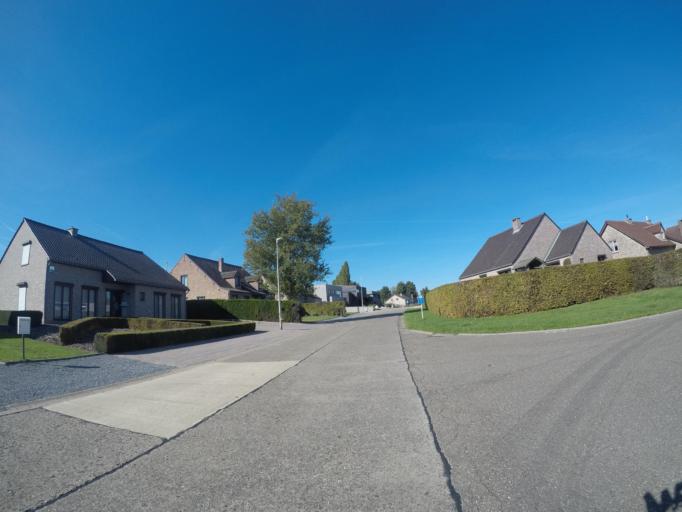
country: BE
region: Flanders
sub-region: Provincie Limburg
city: Alken
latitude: 50.8686
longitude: 5.2721
